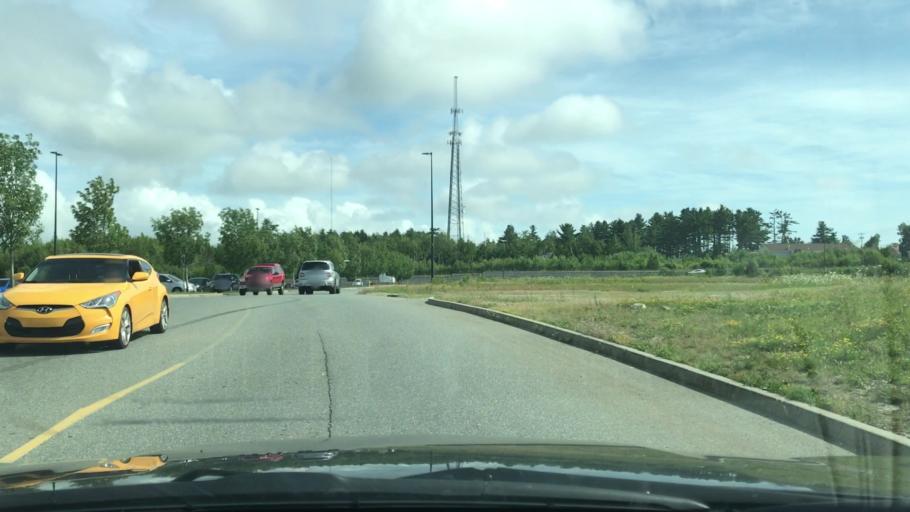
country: US
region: Maine
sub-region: Hancock County
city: Ellsworth
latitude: 44.5253
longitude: -68.3955
